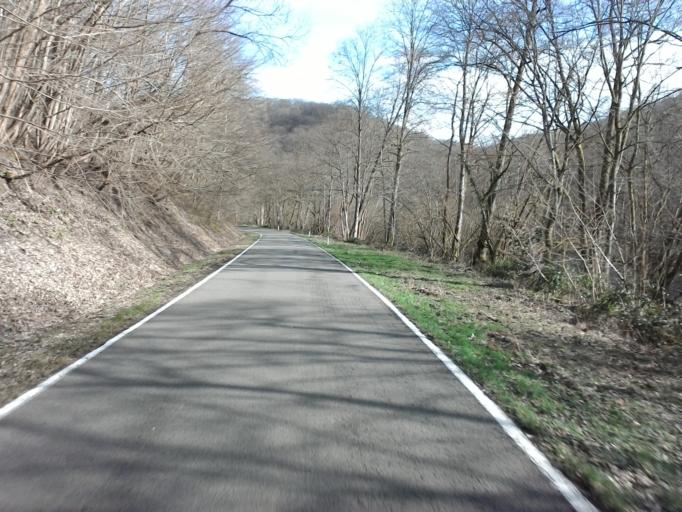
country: BE
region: Wallonia
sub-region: Province du Luxembourg
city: Daverdisse
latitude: 50.0393
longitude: 5.1334
